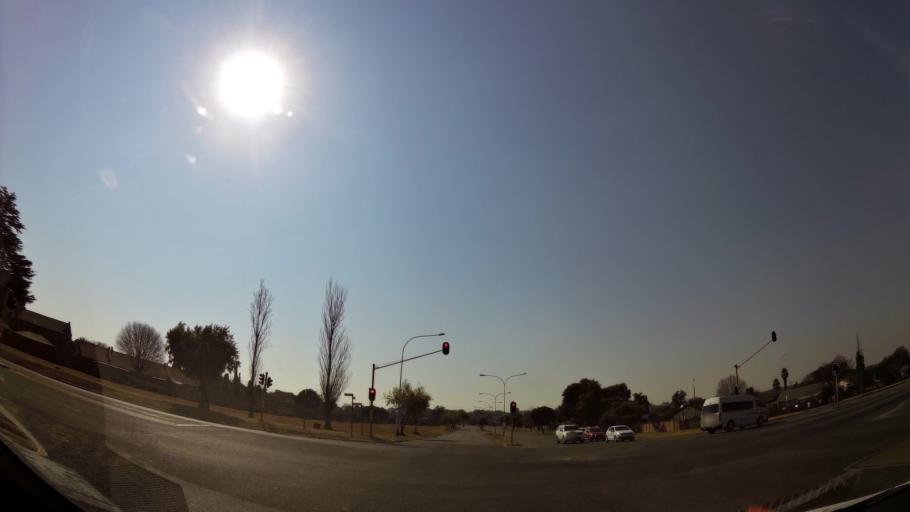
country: ZA
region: Gauteng
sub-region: Ekurhuleni Metropolitan Municipality
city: Boksburg
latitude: -26.2307
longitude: 28.2721
